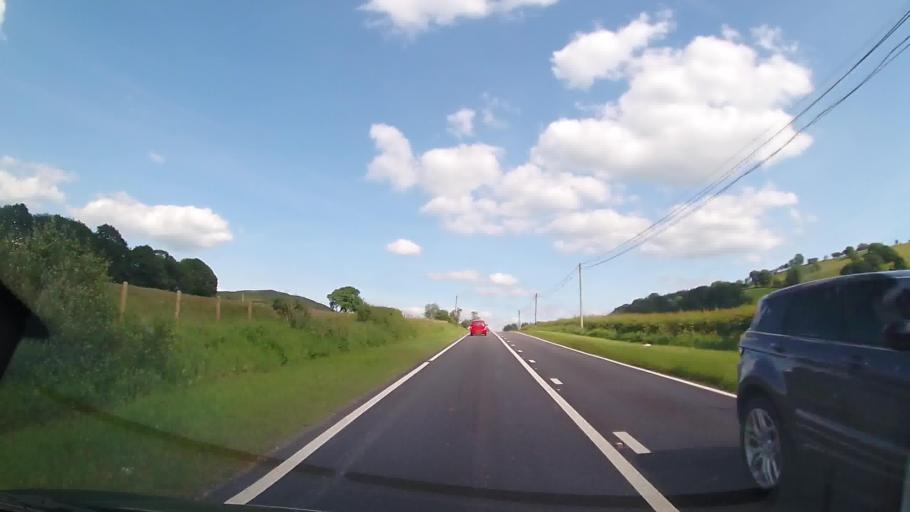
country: GB
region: Wales
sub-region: Sir Powys
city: Llangynog
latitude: 52.6751
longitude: -3.4169
